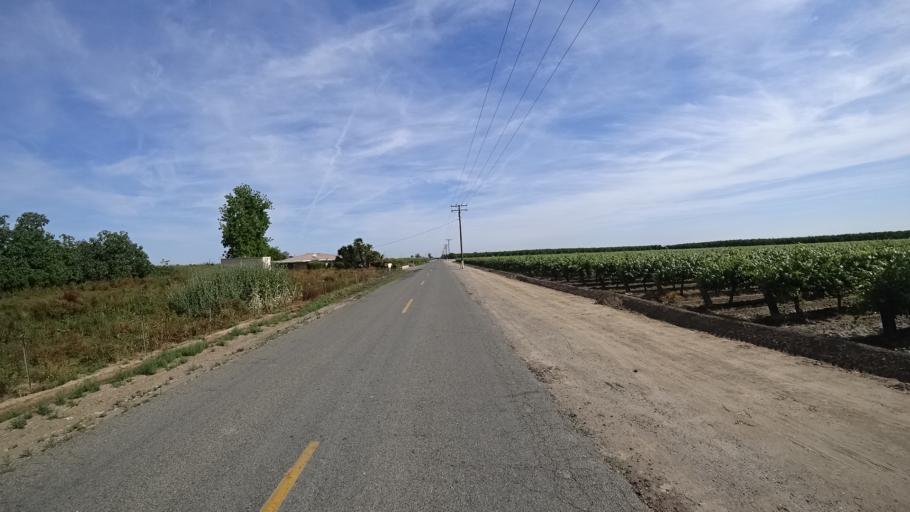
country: US
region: California
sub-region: Kings County
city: Hanford
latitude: 36.3583
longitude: -119.6101
